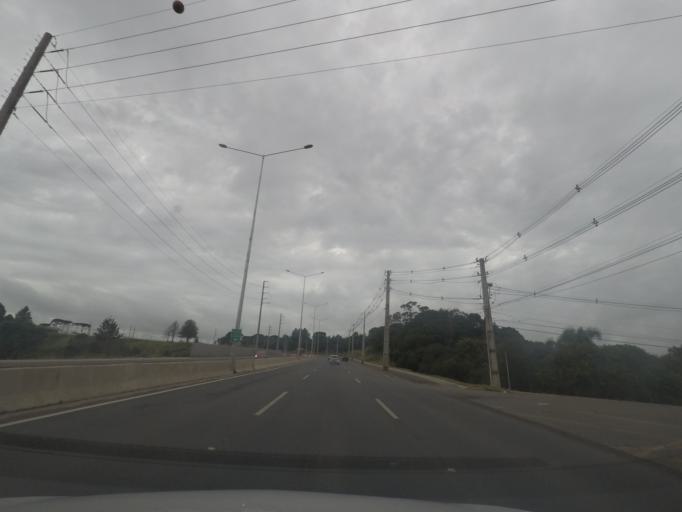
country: BR
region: Parana
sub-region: Piraquara
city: Piraquara
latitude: -25.4600
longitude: -49.0825
